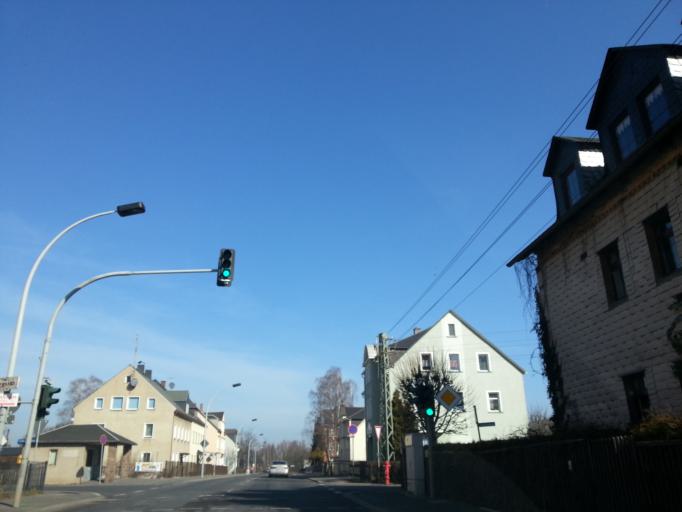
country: DE
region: Saxony
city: Brand-Erbisdorf
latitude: 50.8614
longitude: 13.3202
